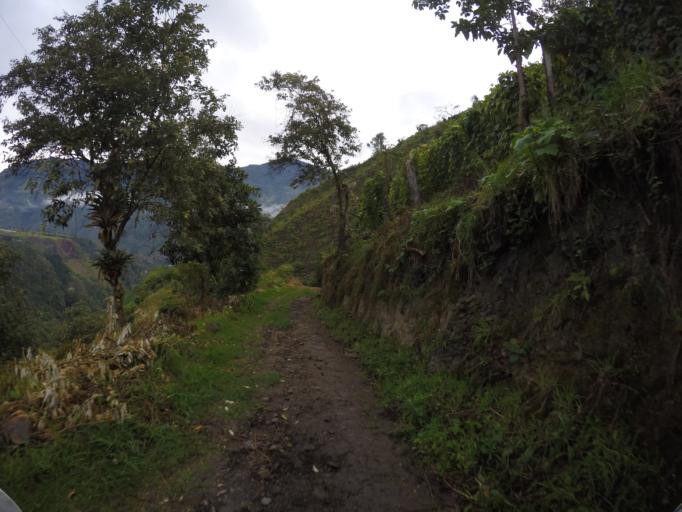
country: CO
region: Tolima
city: Cajamarca
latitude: 4.5070
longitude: -75.3941
